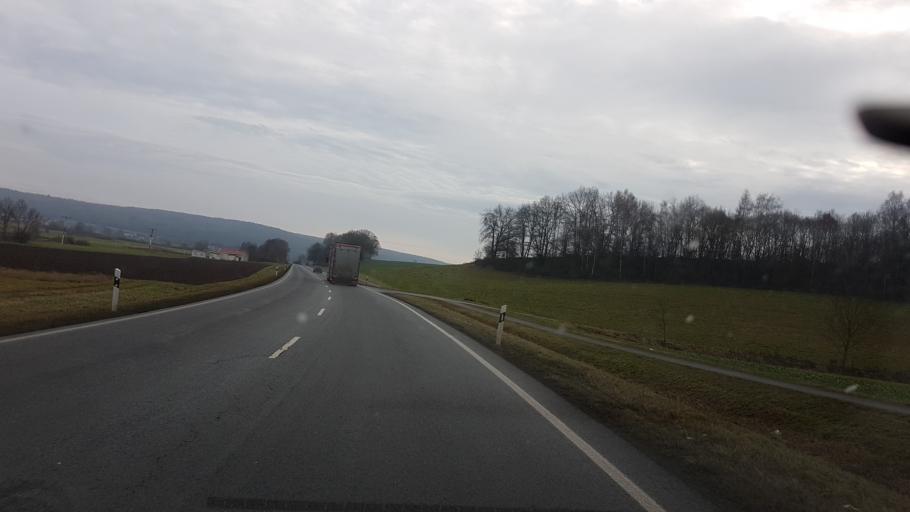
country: DE
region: Bavaria
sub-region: Upper Franconia
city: Gerach
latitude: 50.0428
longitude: 10.8147
